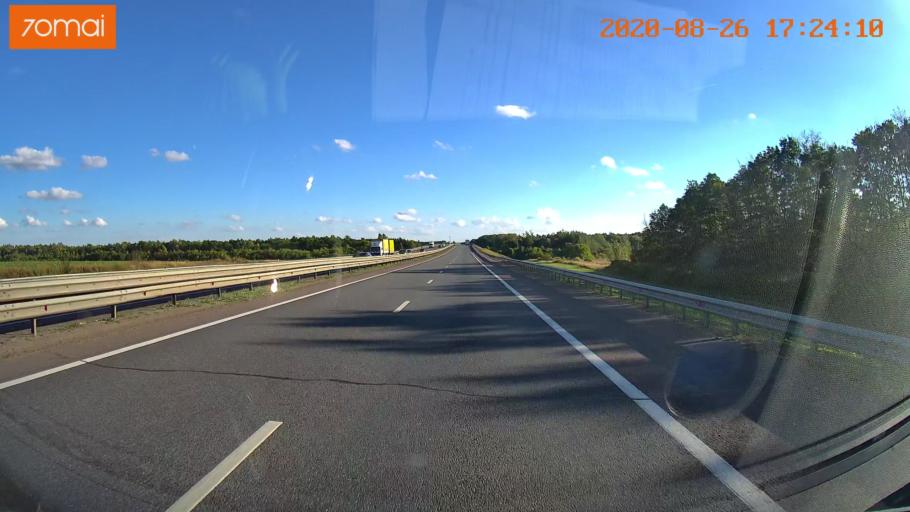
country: RU
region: Tula
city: Volovo
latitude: 53.5222
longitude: 38.1169
